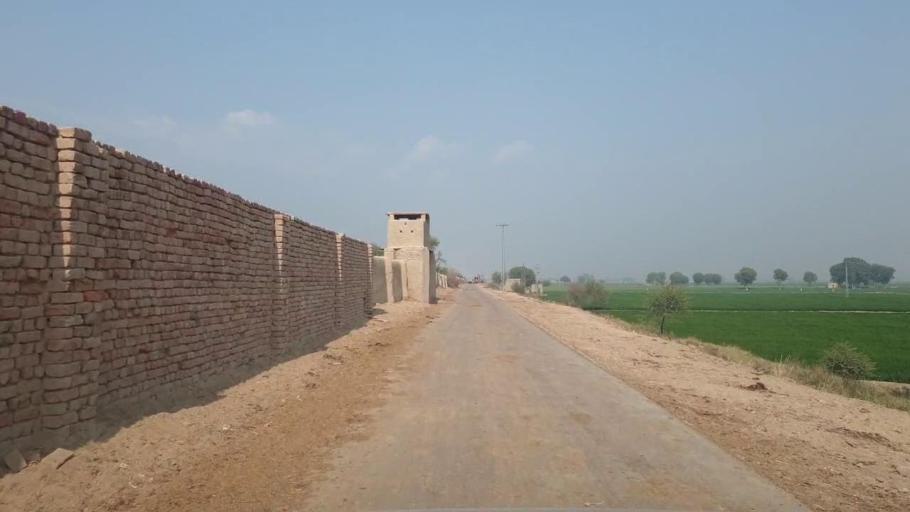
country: PK
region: Sindh
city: Hala
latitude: 25.7868
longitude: 68.4001
